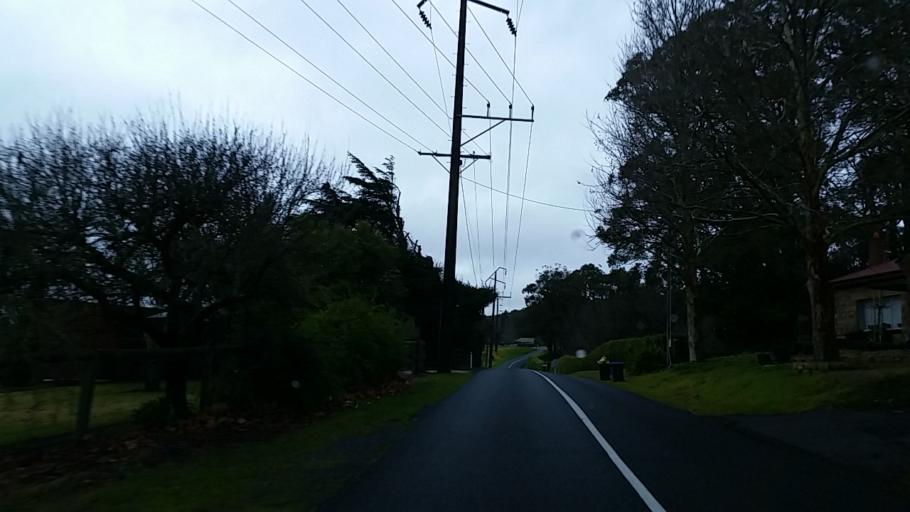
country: AU
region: South Australia
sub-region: Adelaide Hills
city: Bridgewater
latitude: -34.9726
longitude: 138.7365
